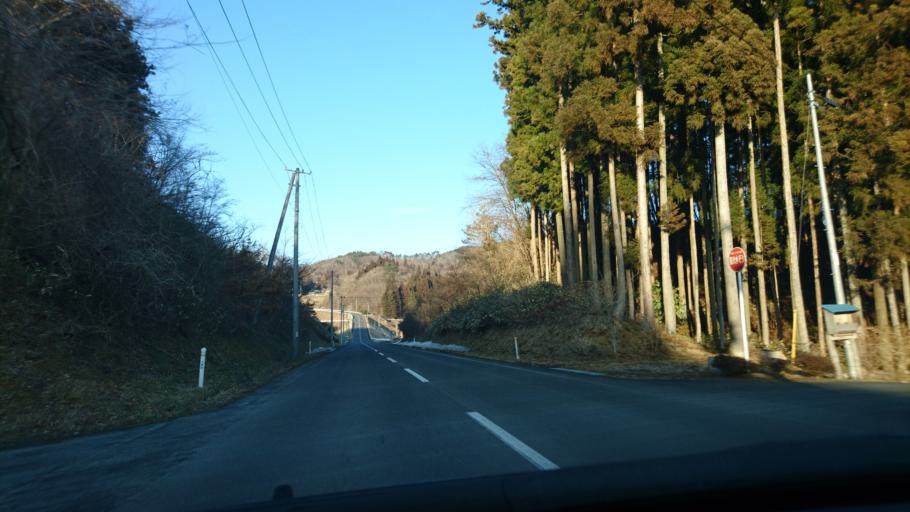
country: JP
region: Iwate
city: Ichinoseki
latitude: 39.0217
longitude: 141.3720
